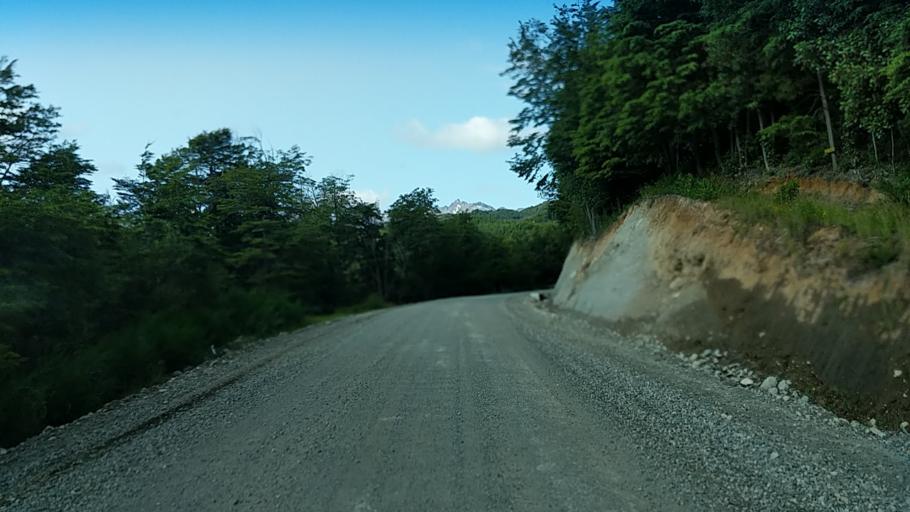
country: CL
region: Los Lagos
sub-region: Provincia de Palena
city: Futaleufu
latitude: -43.2406
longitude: -71.9284
